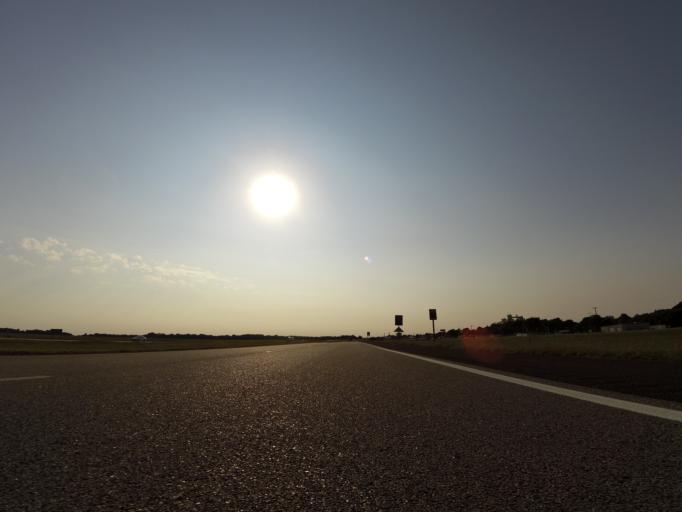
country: US
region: Kansas
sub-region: Reno County
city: Haven
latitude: 37.8952
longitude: -97.7759
